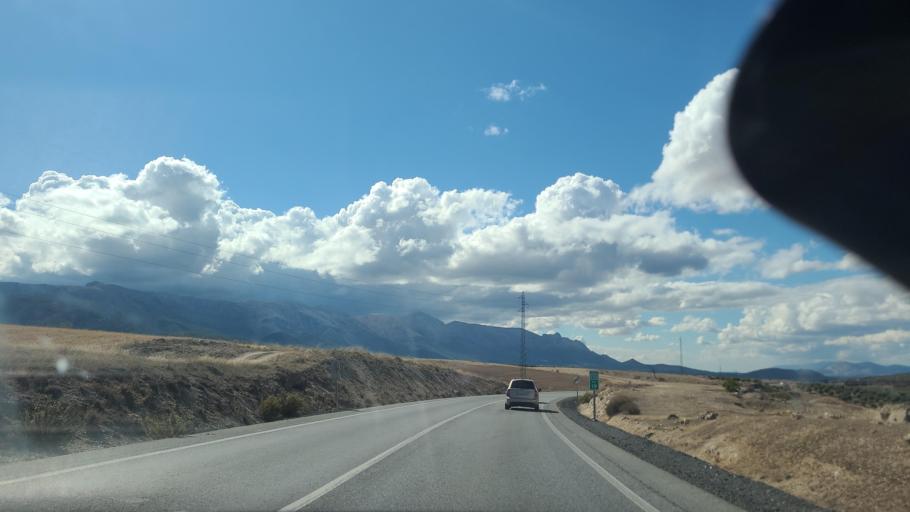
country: ES
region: Andalusia
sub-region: Provincia de Granada
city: Pinar
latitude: 37.4079
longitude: -3.3720
